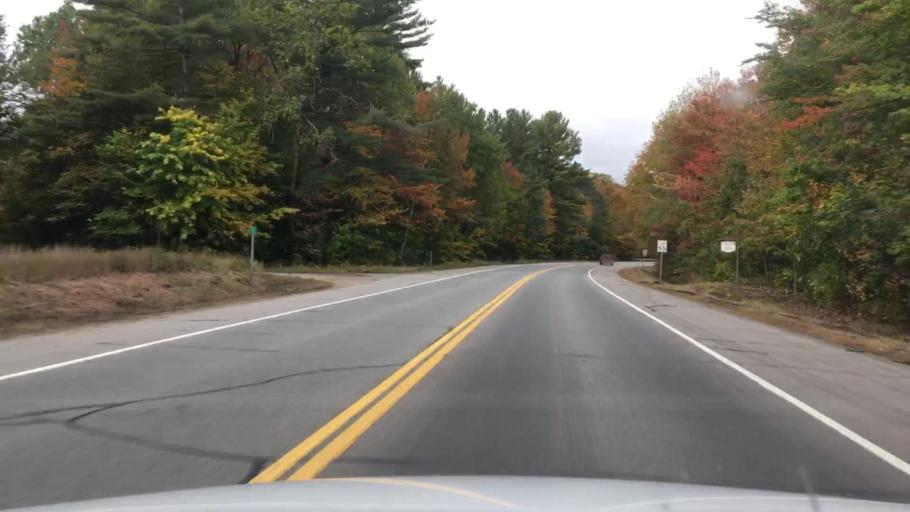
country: US
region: New Hampshire
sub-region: Coos County
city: Gorham
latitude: 44.3850
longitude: -71.0163
